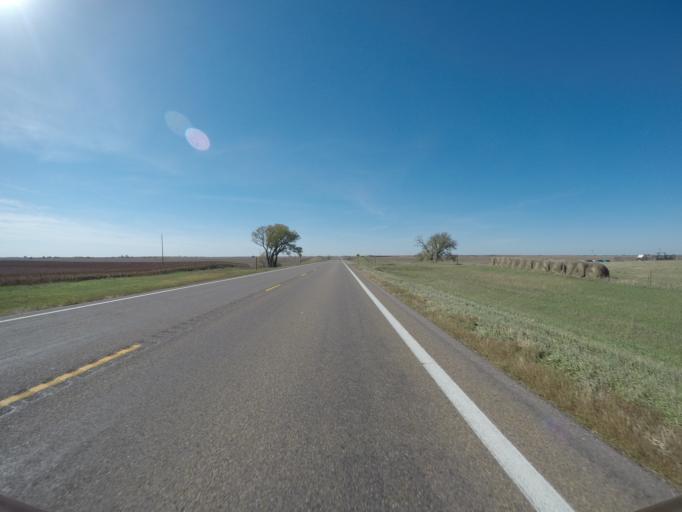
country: US
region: Kansas
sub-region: Smith County
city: Smith Center
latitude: 39.7711
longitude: -98.9596
